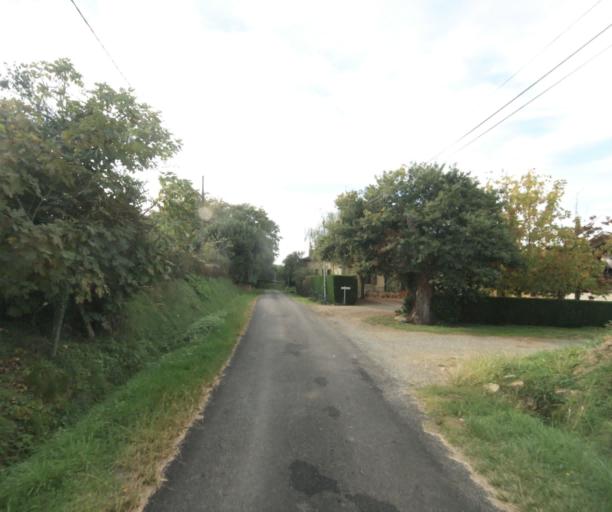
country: FR
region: Midi-Pyrenees
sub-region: Departement du Gers
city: Cazaubon
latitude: 43.8716
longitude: -0.1152
